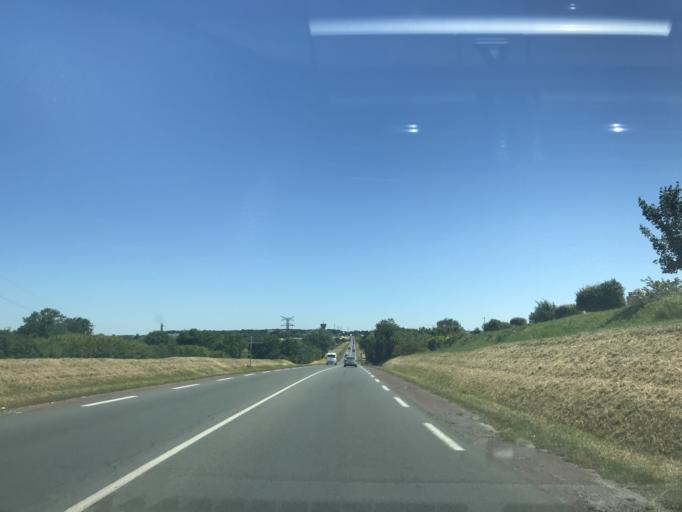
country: FR
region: Poitou-Charentes
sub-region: Departement de la Charente-Maritime
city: Royan
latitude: 45.6378
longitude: -1.0196
